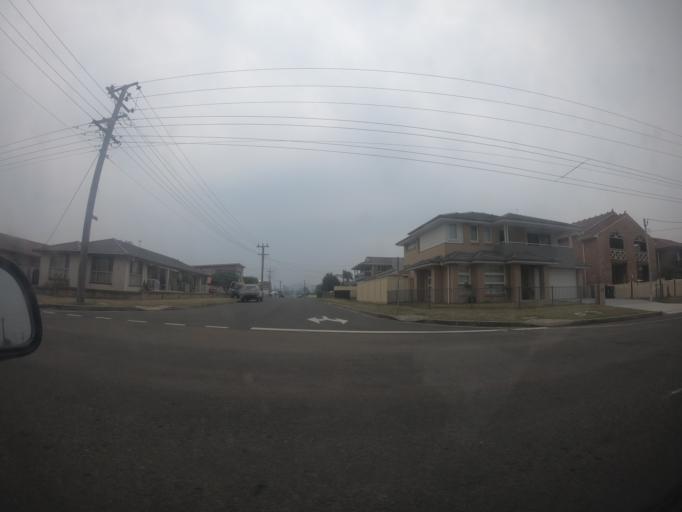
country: AU
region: New South Wales
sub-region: Shellharbour
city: Lake Illawarra
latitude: -34.5511
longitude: 150.8675
